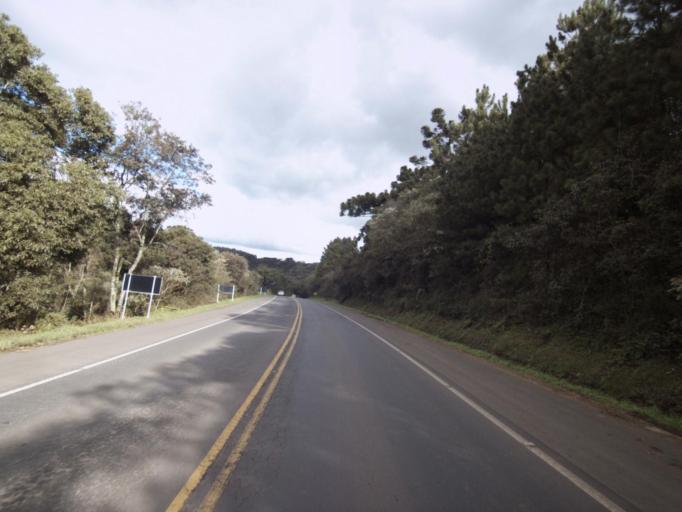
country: BR
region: Santa Catarina
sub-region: Joacaba
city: Joacaba
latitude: -27.0751
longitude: -51.6633
